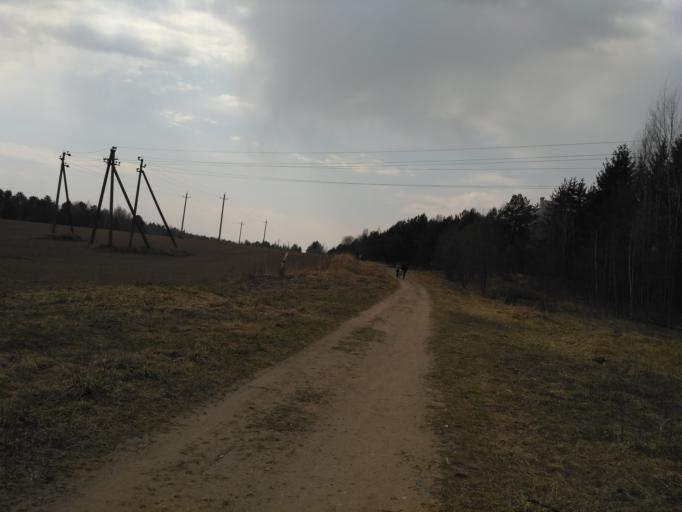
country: BY
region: Minsk
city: Zamostochcha
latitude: 53.8831
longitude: 27.9116
